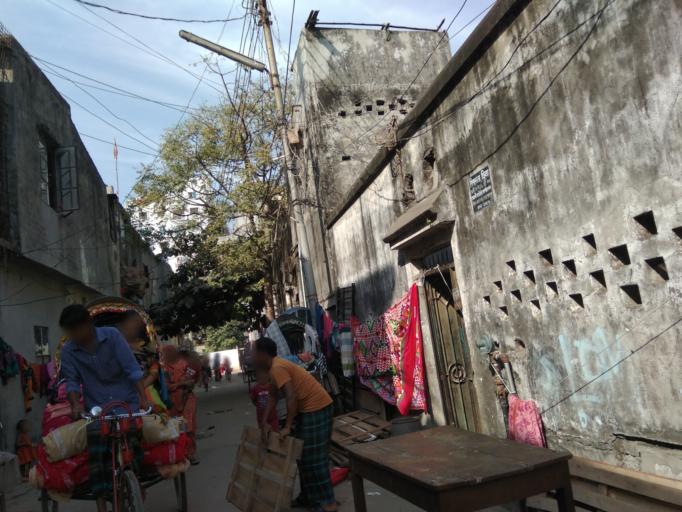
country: BD
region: Dhaka
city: Azimpur
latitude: 23.7758
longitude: 90.3568
